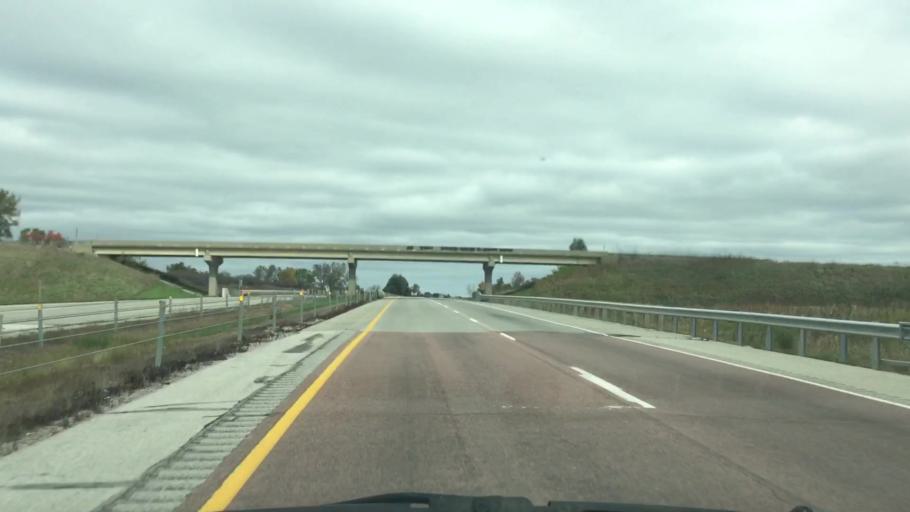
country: US
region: Iowa
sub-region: Clarke County
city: Osceola
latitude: 41.2524
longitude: -93.7808
